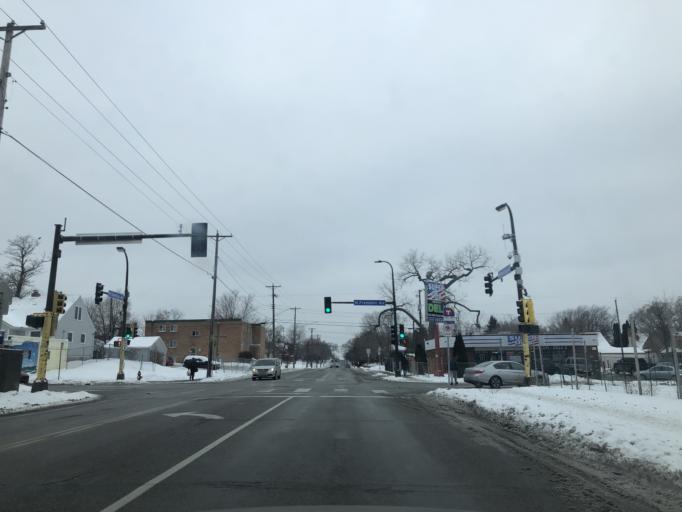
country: US
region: Minnesota
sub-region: Anoka County
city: Columbia Heights
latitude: 45.0240
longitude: -93.2952
